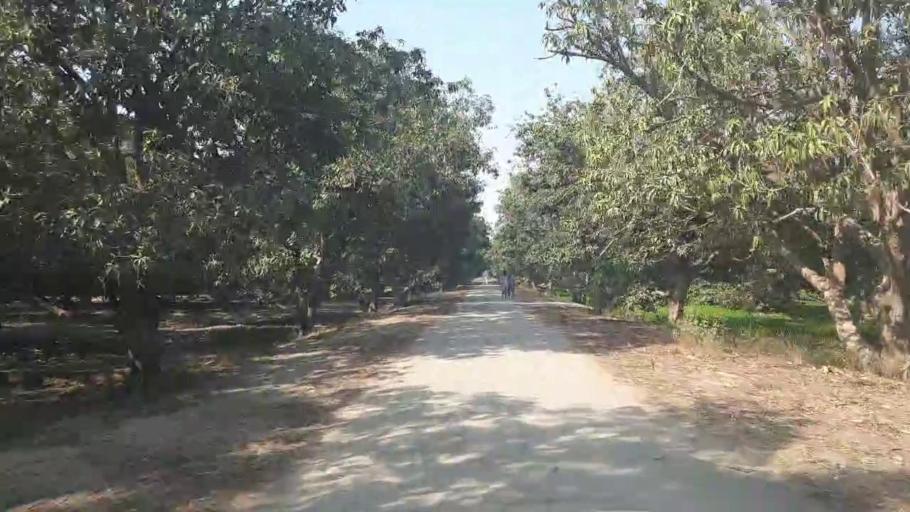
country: PK
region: Sindh
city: Tando Allahyar
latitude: 25.4707
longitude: 68.7815
